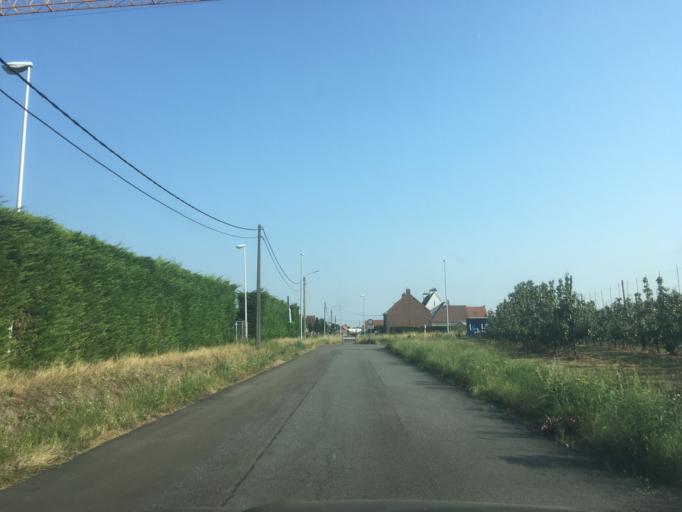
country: BE
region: Flanders
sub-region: Provincie West-Vlaanderen
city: Oostrozebeke
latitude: 50.9090
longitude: 3.3430
